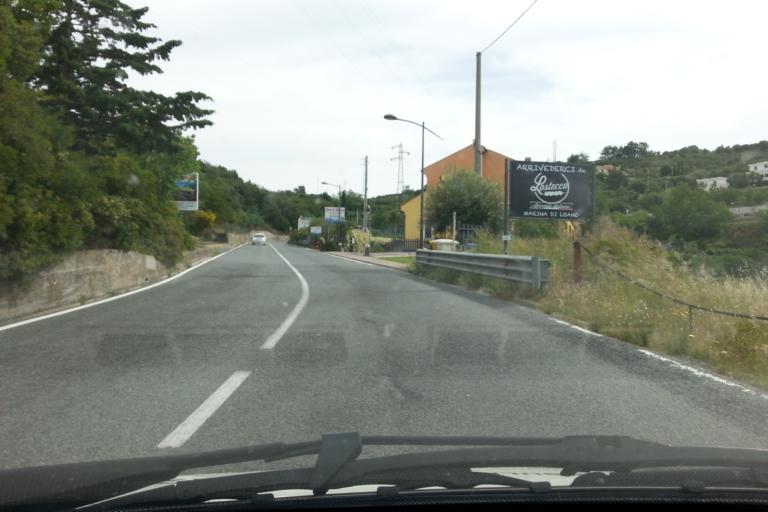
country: IT
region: Liguria
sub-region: Provincia di Savona
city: Pietra Ligure
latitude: 44.1542
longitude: 8.2684
